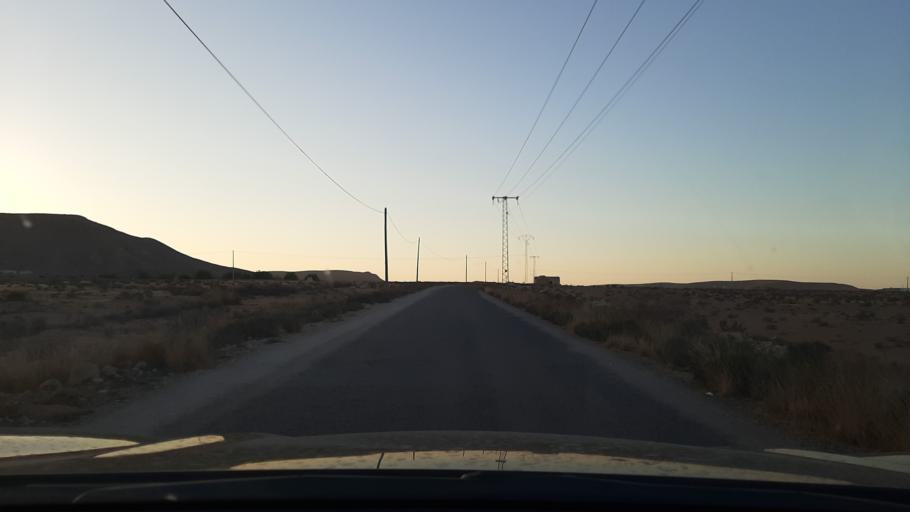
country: TN
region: Qabis
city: Matmata
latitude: 33.5490
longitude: 10.1895
